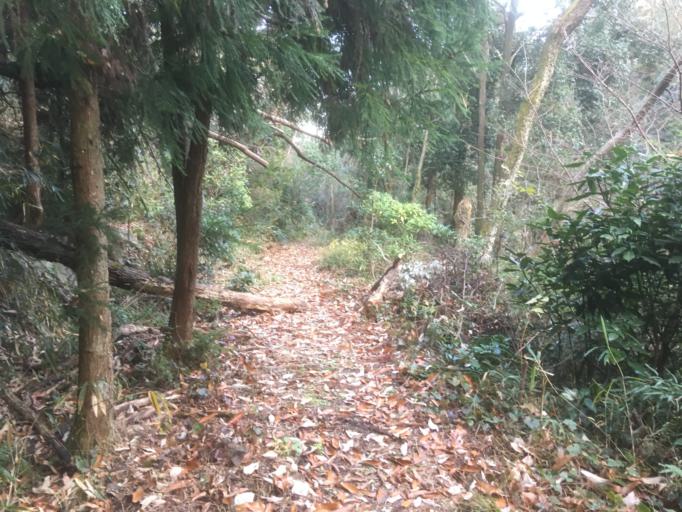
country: JP
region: Nara
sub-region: Ikoma-shi
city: Ikoma
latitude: 34.6971
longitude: 135.6889
